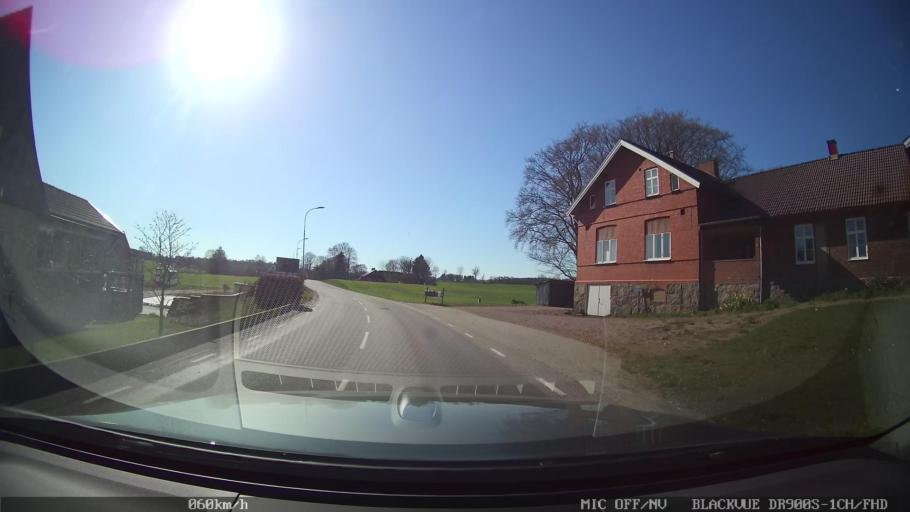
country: SE
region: Skane
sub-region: Klippans Kommun
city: Ljungbyhed
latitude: 55.9638
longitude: 13.2471
